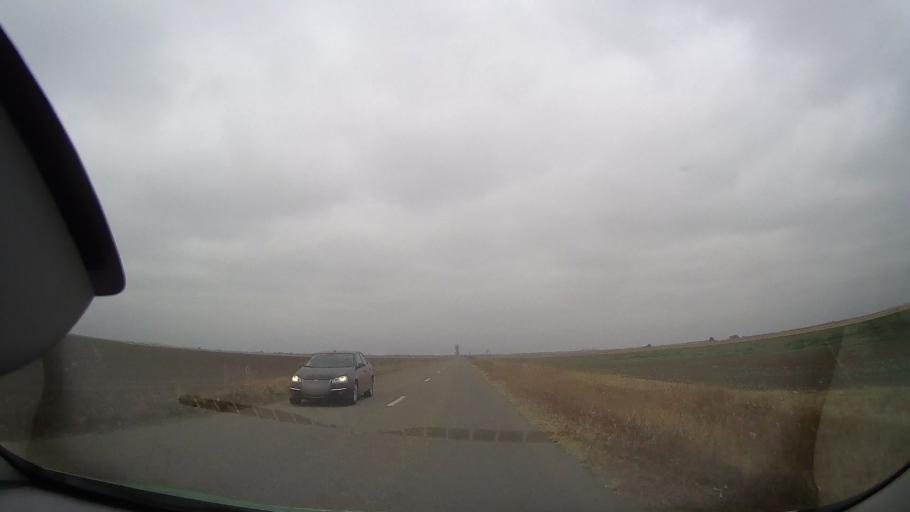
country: RO
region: Buzau
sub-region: Comuna Bradeanu
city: Bradeanu
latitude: 44.8987
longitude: 26.8725
